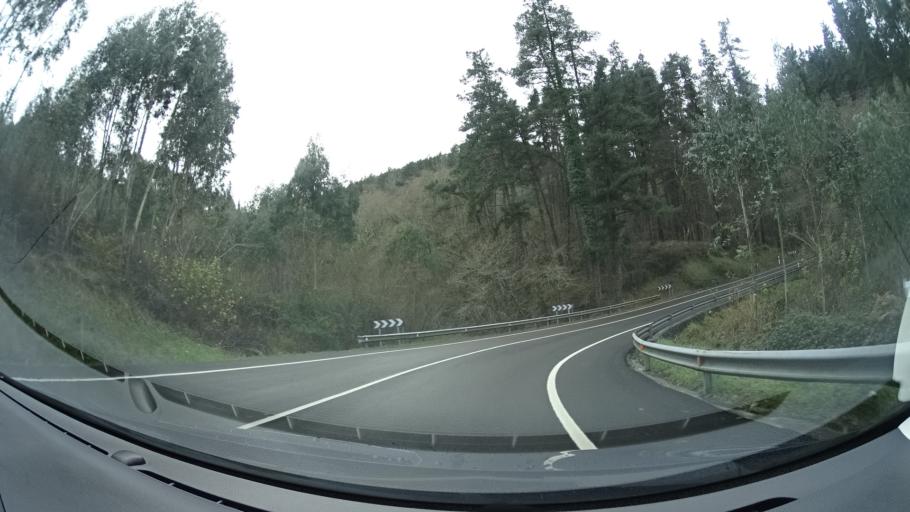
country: ES
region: Basque Country
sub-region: Bizkaia
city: Bakio
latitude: 43.3821
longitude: -2.7736
